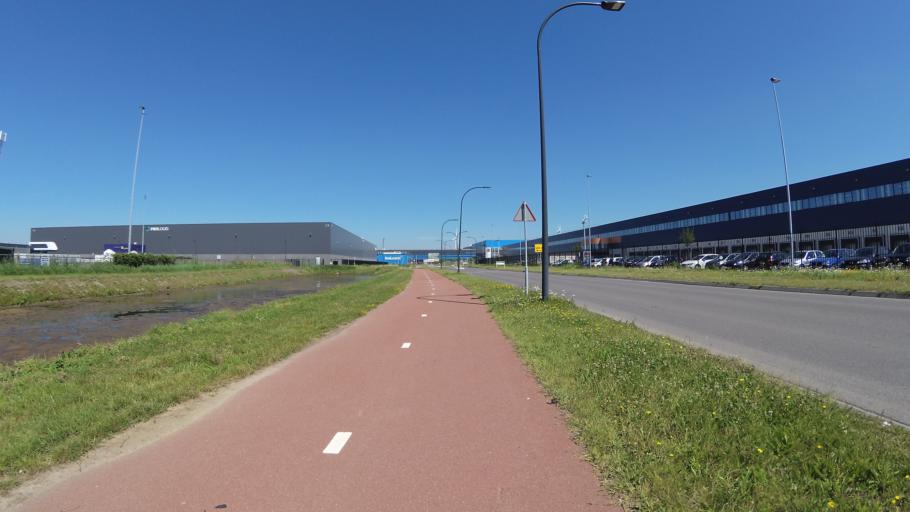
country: NL
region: North Brabant
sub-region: Gemeente Waalwijk
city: Waalwijk
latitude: 51.6985
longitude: 5.0685
